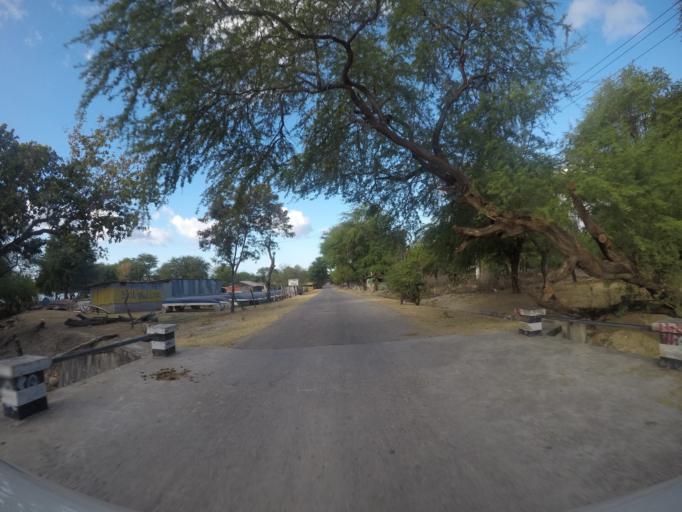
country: TL
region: Lautem
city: Lospalos
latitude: -8.3565
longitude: 126.9113
